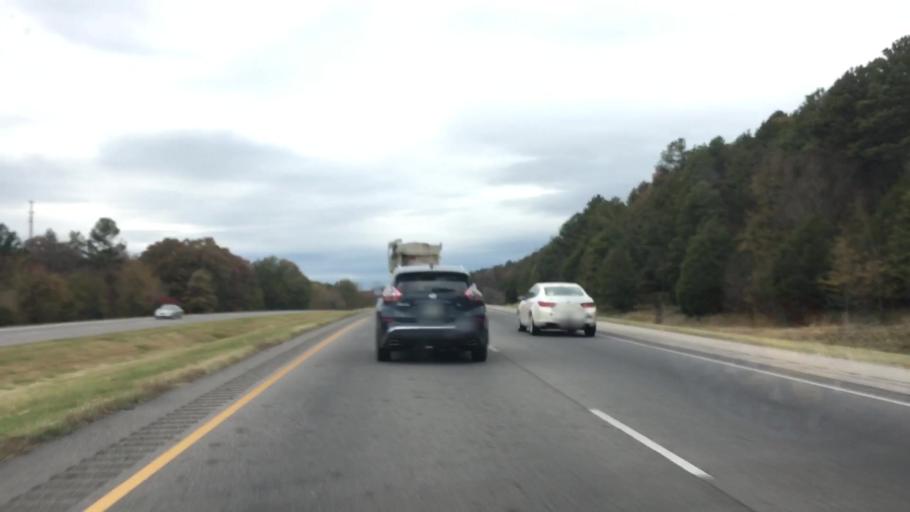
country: US
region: Arkansas
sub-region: Johnson County
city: Coal Hill
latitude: 35.5007
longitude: -93.7223
